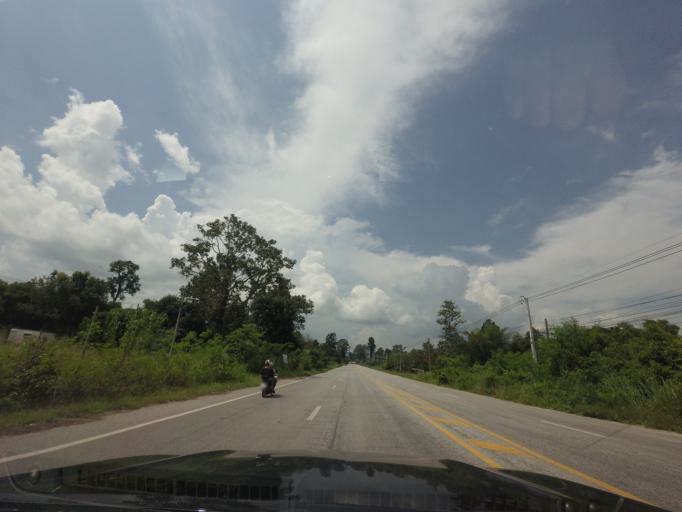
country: TH
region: Khon Kaen
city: Wiang Kao
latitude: 16.6704
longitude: 102.3142
